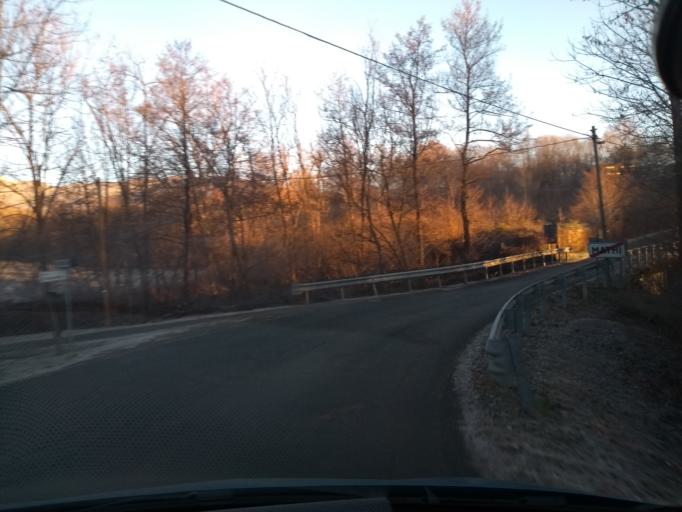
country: IT
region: Piedmont
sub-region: Provincia di Torino
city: Corio
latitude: 45.2872
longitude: 7.5474
